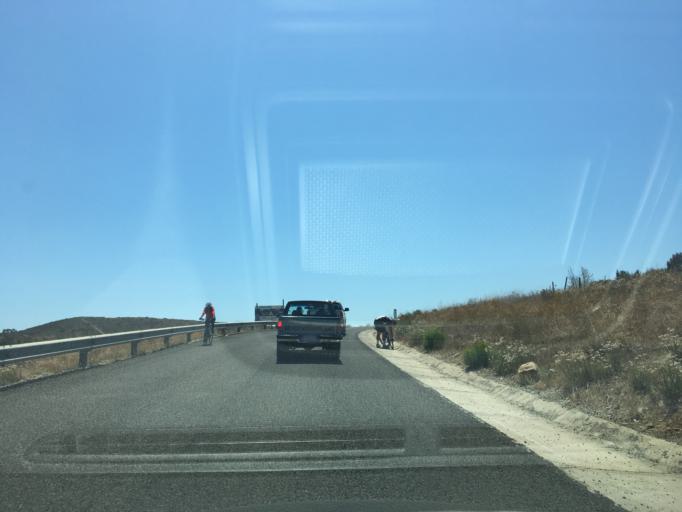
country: MX
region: Baja California
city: El Sauzal
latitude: 31.9940
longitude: -116.6889
